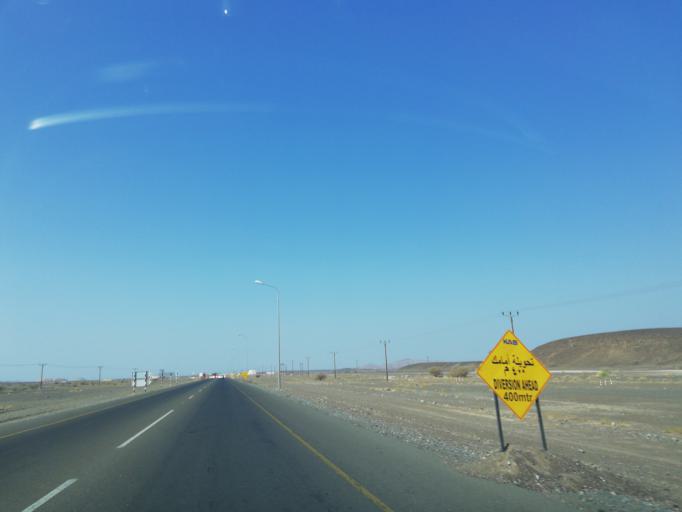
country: OM
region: Ash Sharqiyah
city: Ibra'
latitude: 22.7143
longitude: 58.1457
